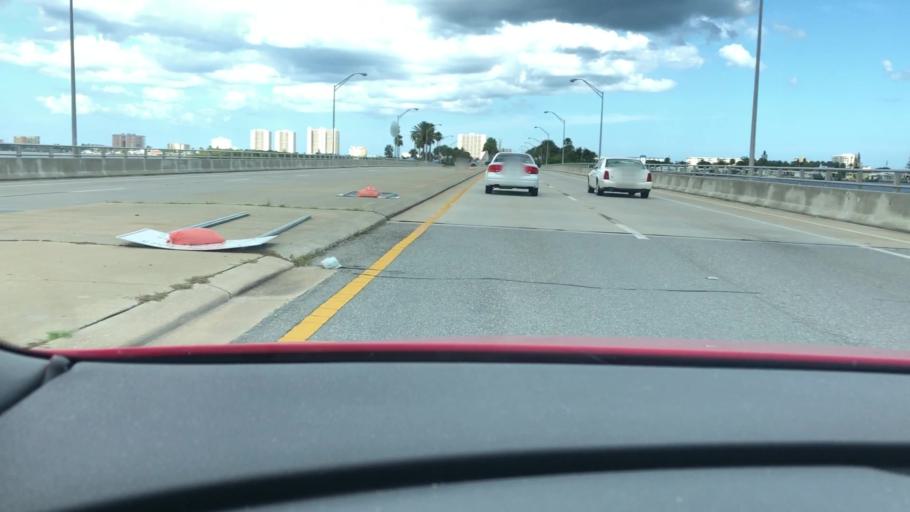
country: US
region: Florida
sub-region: Volusia County
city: Port Orange
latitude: 29.1253
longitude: -80.9816
